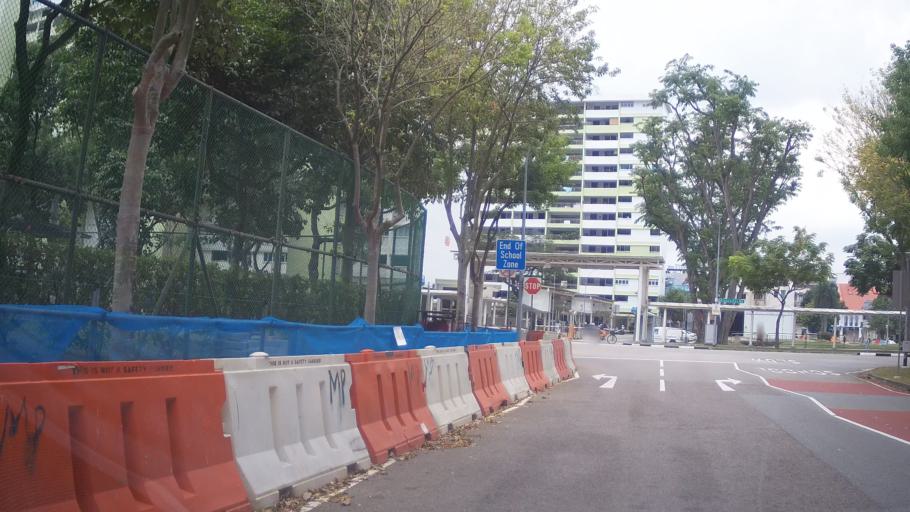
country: SG
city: Singapore
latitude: 1.3126
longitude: 103.8517
